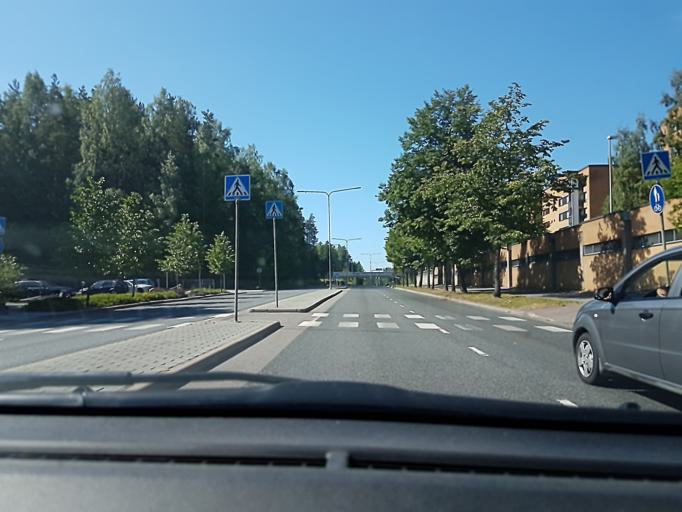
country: FI
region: Uusimaa
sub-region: Helsinki
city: Vantaa
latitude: 60.3221
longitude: 25.0539
